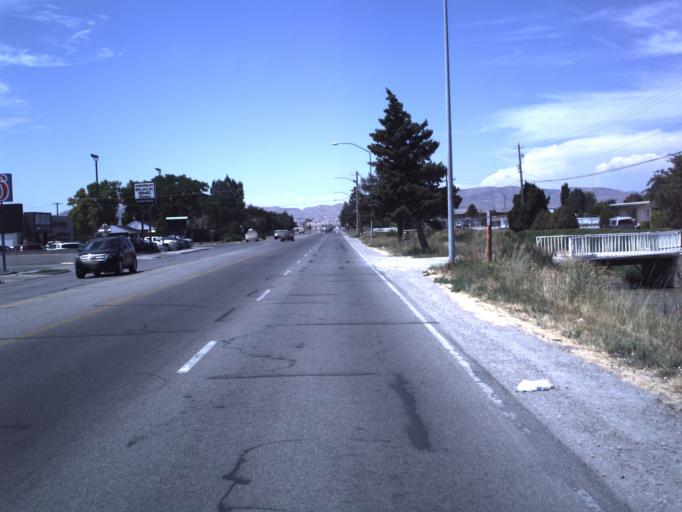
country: US
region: Utah
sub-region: Box Elder County
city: Tremonton
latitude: 41.7116
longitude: -112.1734
